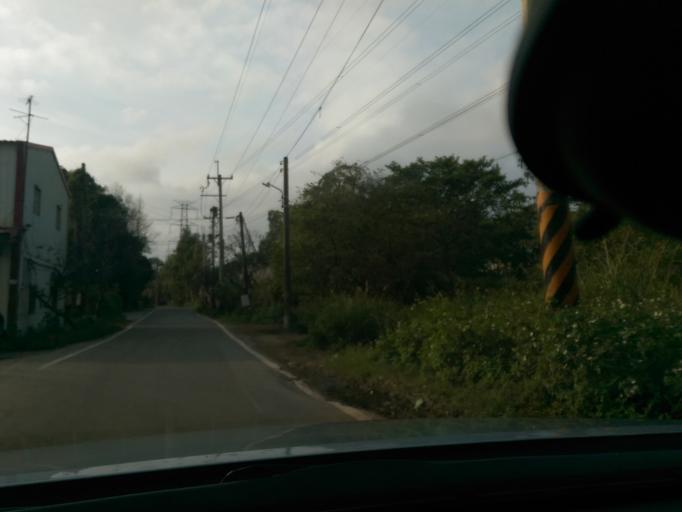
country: TW
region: Taiwan
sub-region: Taoyuan
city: Taoyuan
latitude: 25.0912
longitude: 121.3659
